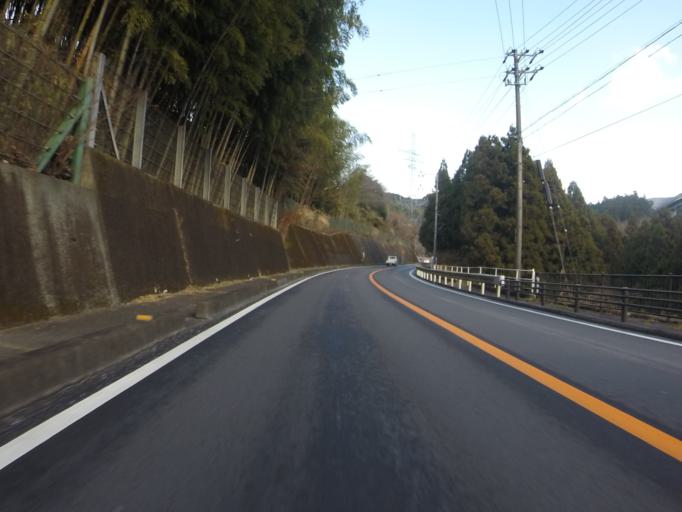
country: JP
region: Shizuoka
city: Fujinomiya
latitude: 35.1475
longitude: 138.5224
